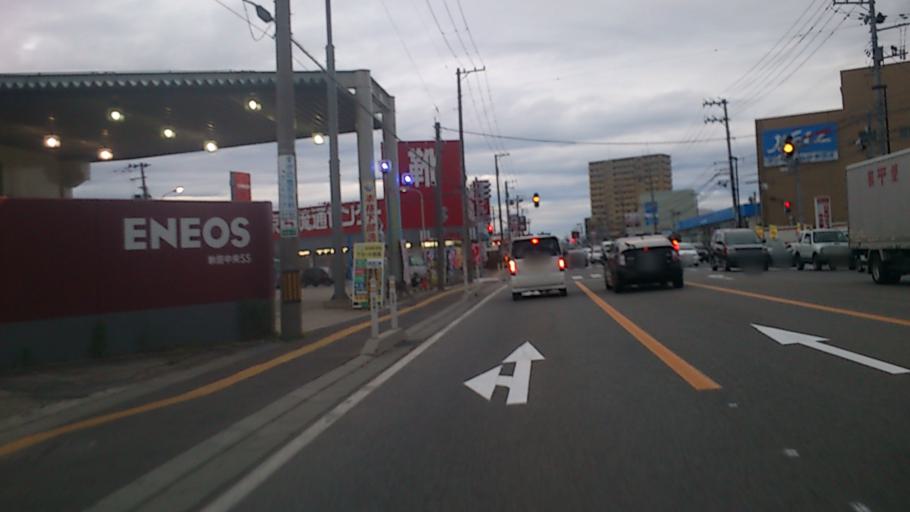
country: JP
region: Akita
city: Akita Shi
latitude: 39.7393
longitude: 140.0958
